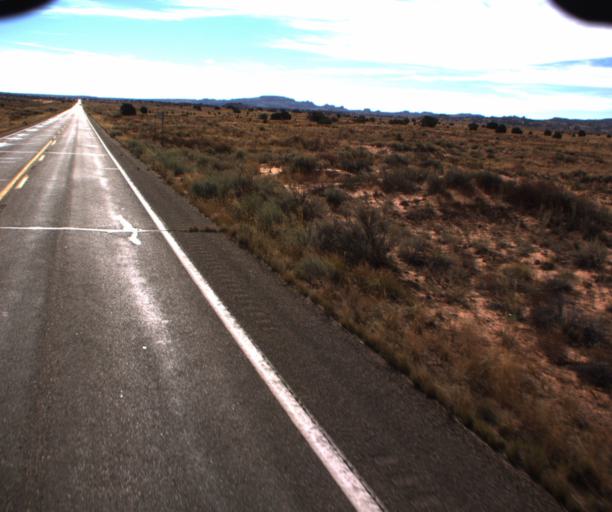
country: US
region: Arizona
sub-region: Coconino County
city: Kaibito
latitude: 36.6137
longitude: -111.1890
